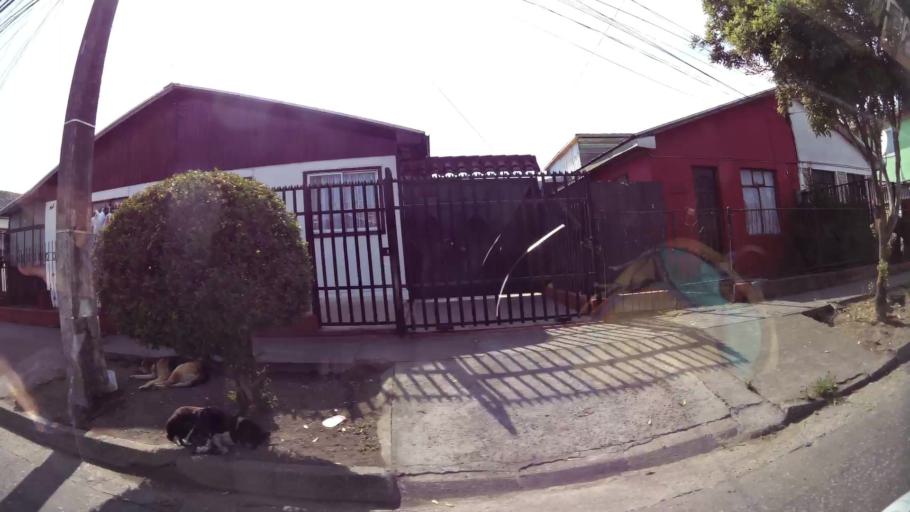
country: CL
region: Biobio
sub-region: Provincia de Concepcion
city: Talcahuano
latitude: -36.7851
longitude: -73.1016
